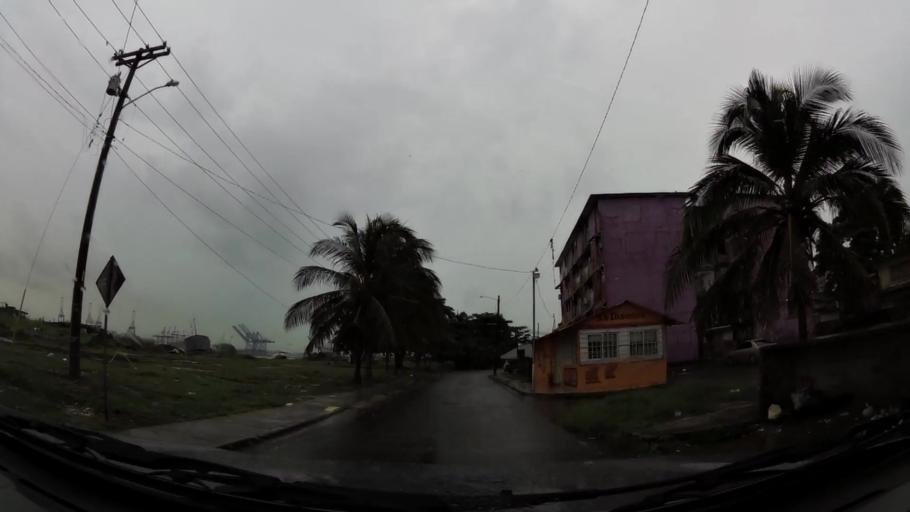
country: PA
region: Colon
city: Colon
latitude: 9.3663
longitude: -79.9008
